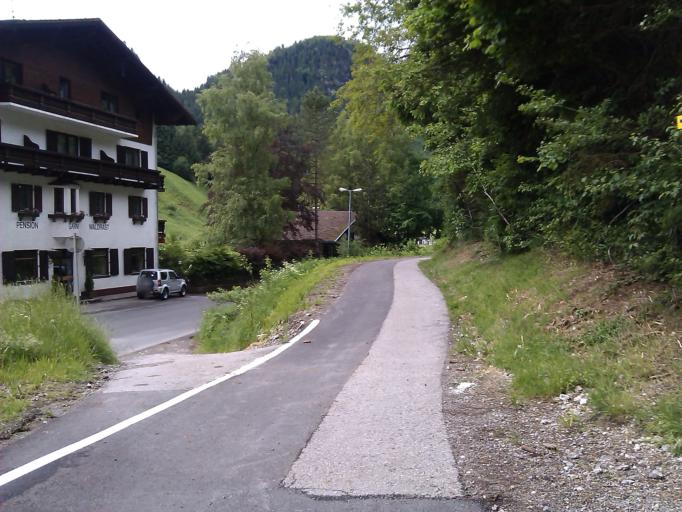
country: AT
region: Tyrol
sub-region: Politischer Bezirk Reutte
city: Reutte
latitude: 47.4742
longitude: 10.7221
